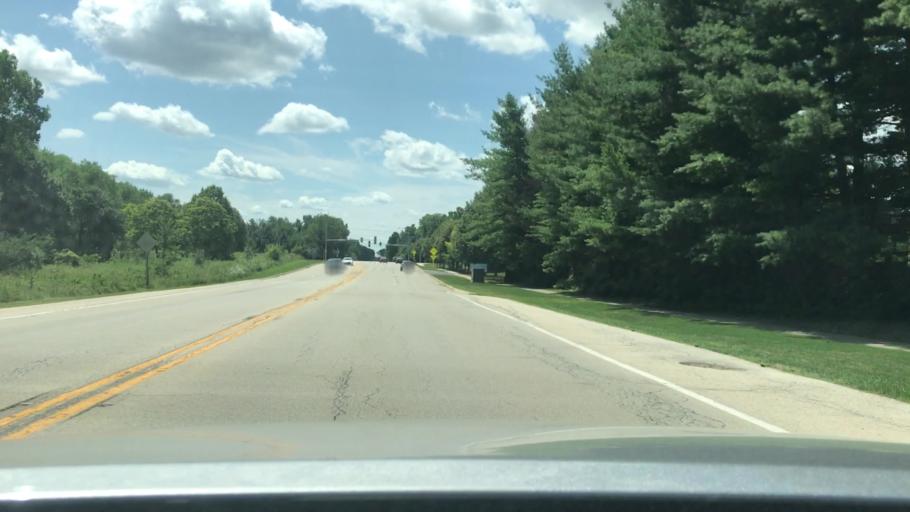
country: US
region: Illinois
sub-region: DuPage County
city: Naperville
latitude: 41.7579
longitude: -88.1040
